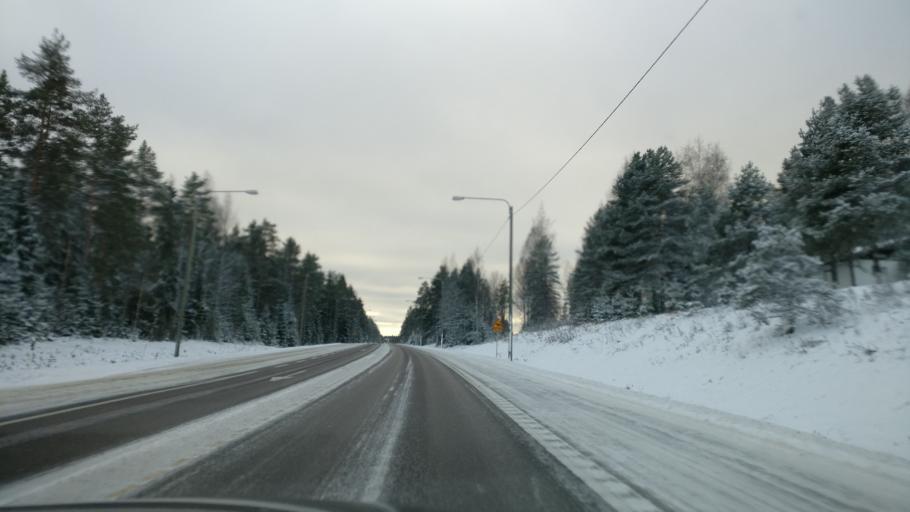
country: FI
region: Paijanne Tavastia
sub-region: Lahti
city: Heinola
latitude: 61.3304
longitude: 26.1620
